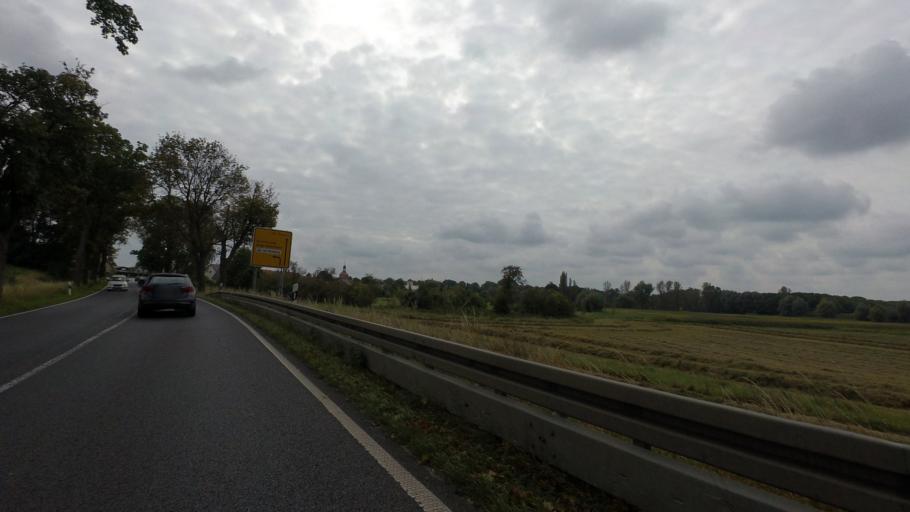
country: DE
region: Brandenburg
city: Rangsdorf
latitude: 52.2791
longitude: 13.4633
